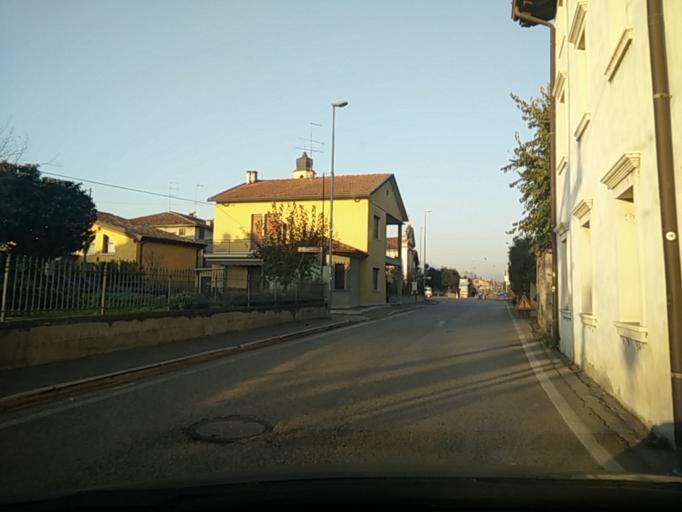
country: IT
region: Veneto
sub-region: Provincia di Verona
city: Salionze
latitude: 45.4032
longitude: 10.7210
